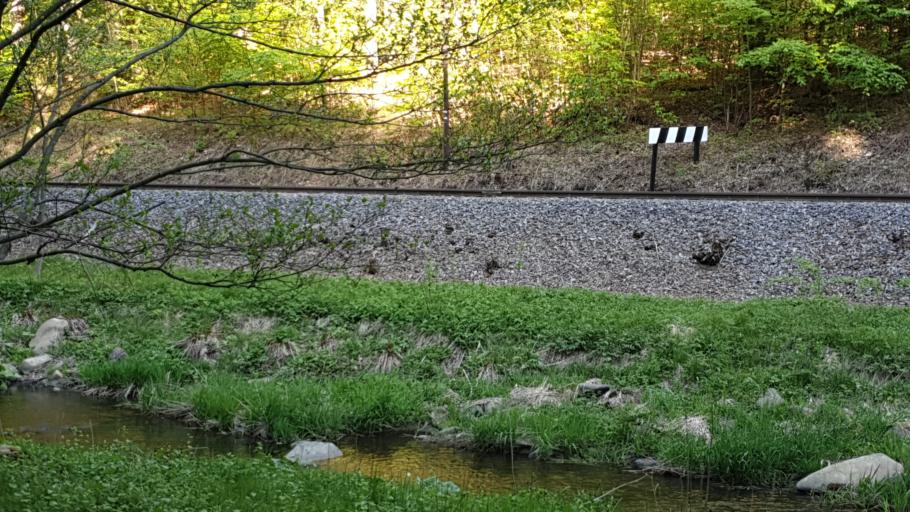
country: DE
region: Saxony
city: Johstadt
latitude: 50.5524
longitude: 13.1431
